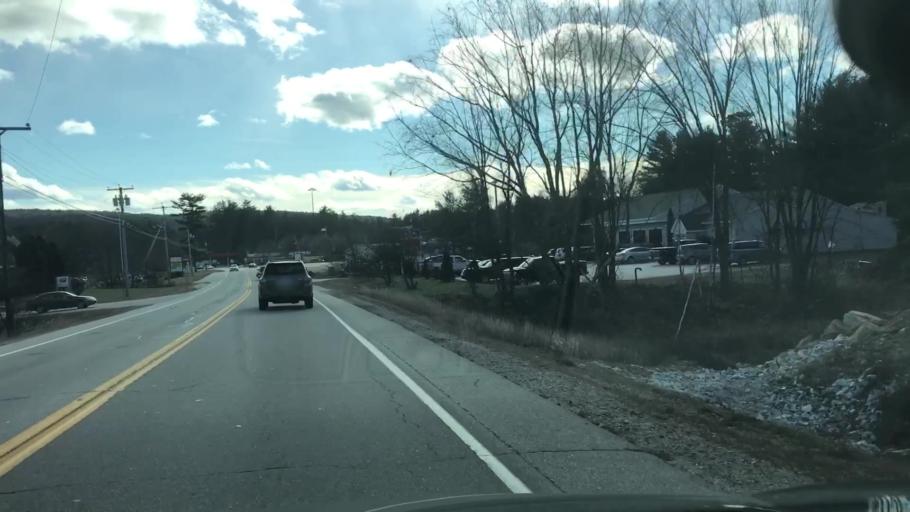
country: US
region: New Hampshire
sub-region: Merrimack County
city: Epsom
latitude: 43.2309
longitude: -71.3611
